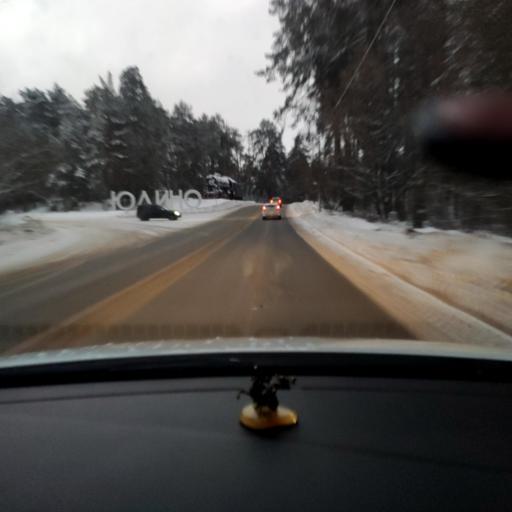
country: RU
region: Tatarstan
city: Osinovo
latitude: 55.8270
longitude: 48.8960
